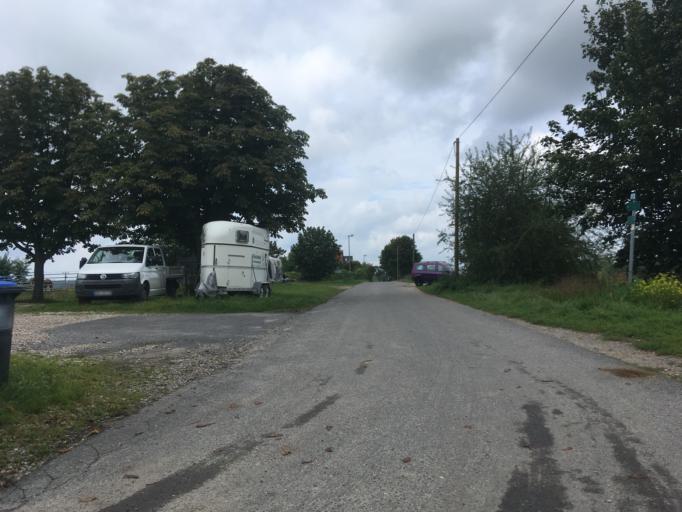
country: DE
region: Brandenburg
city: Glienicke
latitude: 52.6438
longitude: 13.3395
